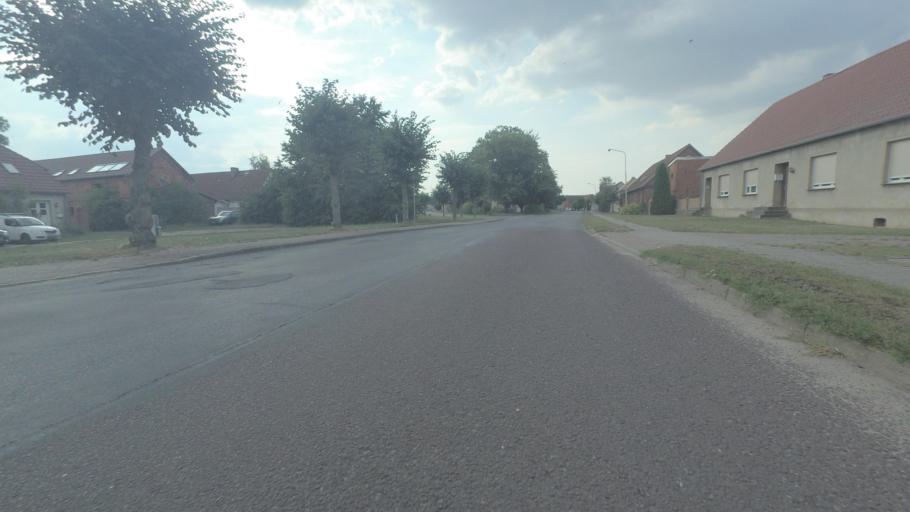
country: DE
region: Brandenburg
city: Wittstock
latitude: 53.2424
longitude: 12.4253
